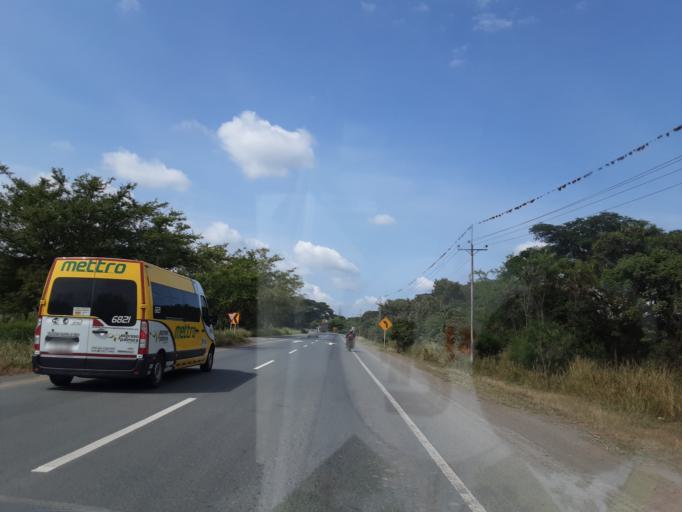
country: CO
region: Valle del Cauca
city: Guacari
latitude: 3.7716
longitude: -76.3269
